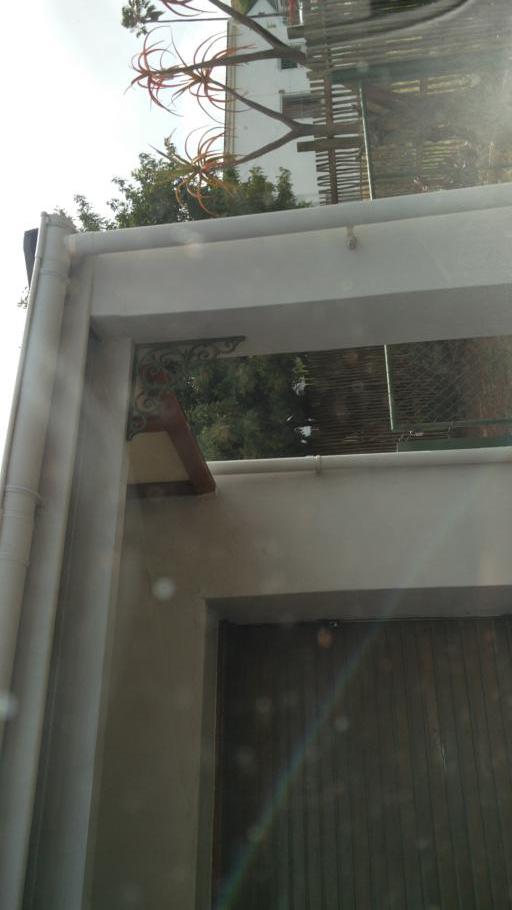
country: ZA
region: Western Cape
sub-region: City of Cape Town
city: Atlantis
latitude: -33.3752
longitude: 18.3783
